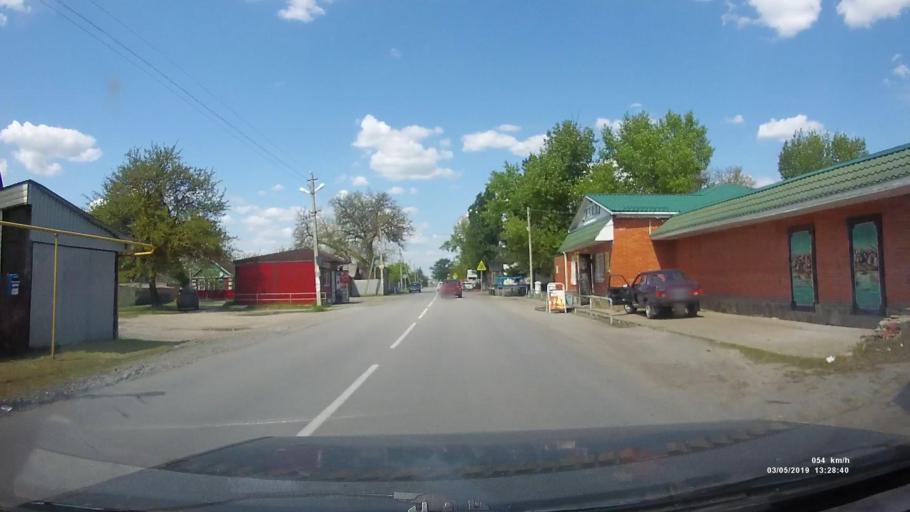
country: RU
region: Rostov
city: Semikarakorsk
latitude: 47.5776
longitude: 40.8417
